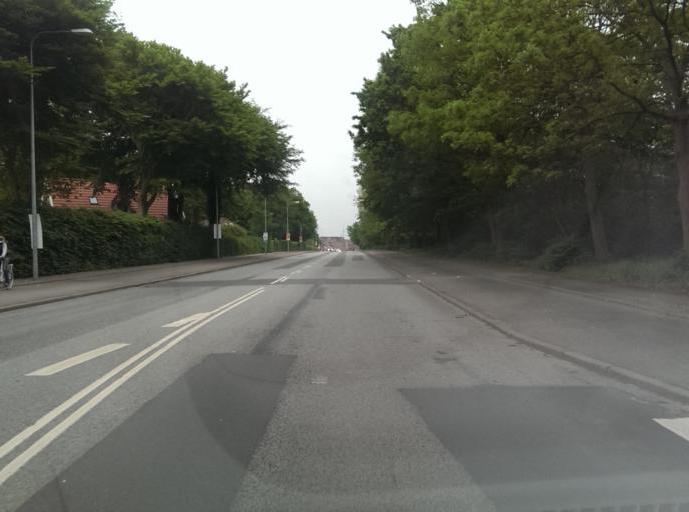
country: DK
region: South Denmark
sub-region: Esbjerg Kommune
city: Esbjerg
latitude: 55.4786
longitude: 8.4303
